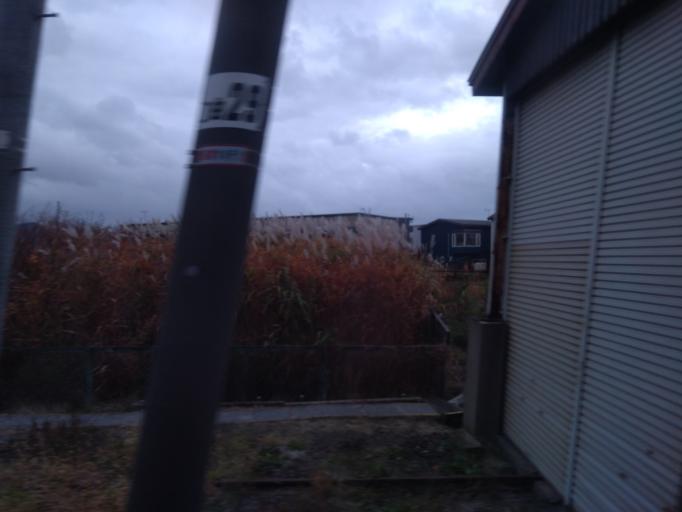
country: JP
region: Hokkaido
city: Hakodate
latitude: 41.8067
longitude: 140.7328
